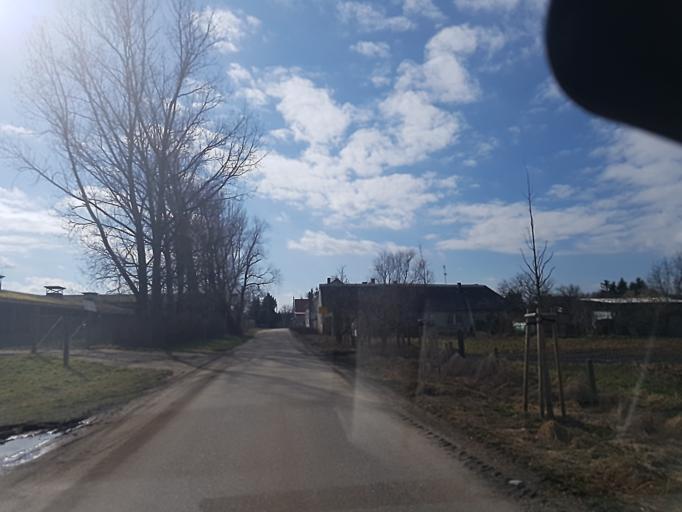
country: DE
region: Brandenburg
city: Schonborn
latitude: 51.5705
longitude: 13.5216
